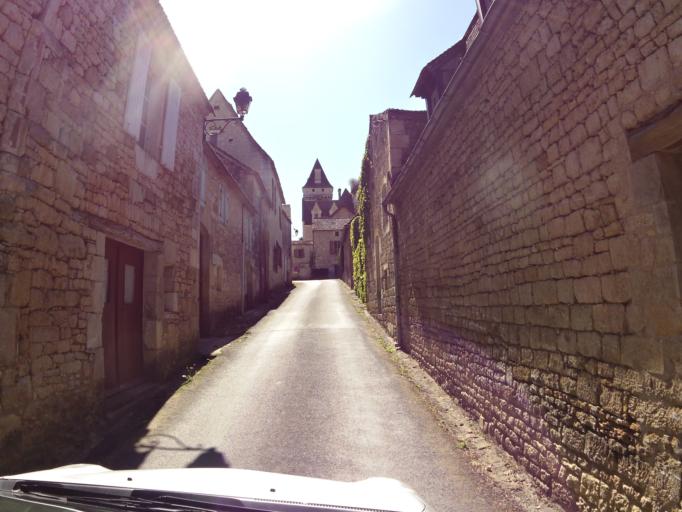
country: FR
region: Aquitaine
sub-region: Departement de la Dordogne
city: Saint-Cyprien
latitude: 44.8241
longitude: 1.1148
